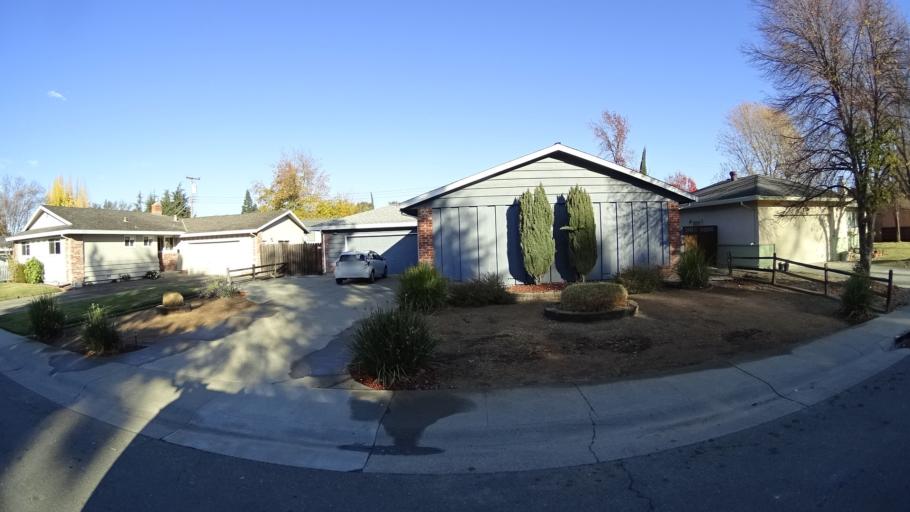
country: US
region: California
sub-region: Sacramento County
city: Antelope
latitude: 38.6739
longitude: -121.3114
